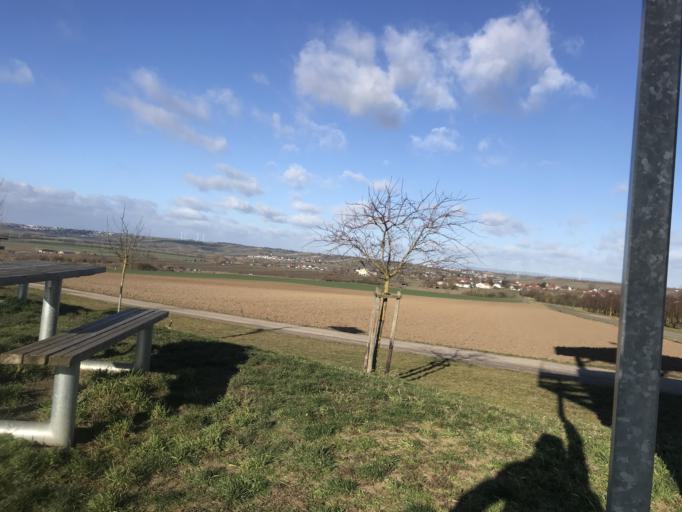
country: DE
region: Rheinland-Pfalz
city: Lorzweiler
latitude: 49.8924
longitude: 8.3111
